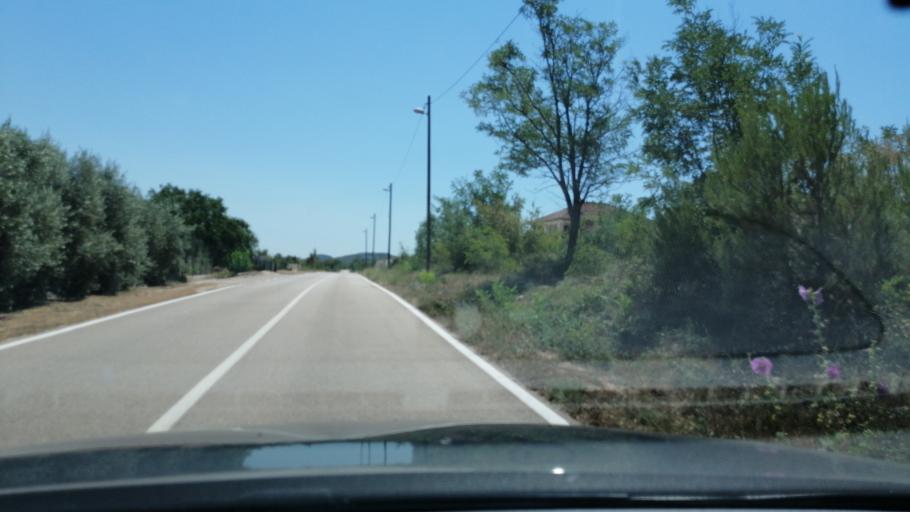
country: HR
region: Sibensko-Kniniska
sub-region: Grad Sibenik
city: Pirovac
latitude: 43.8691
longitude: 15.6818
